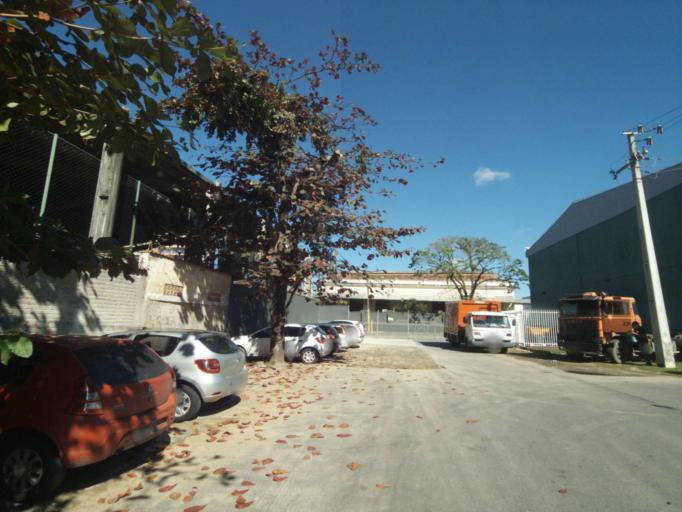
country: BR
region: Parana
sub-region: Paranagua
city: Paranagua
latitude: -25.5162
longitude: -48.5061
